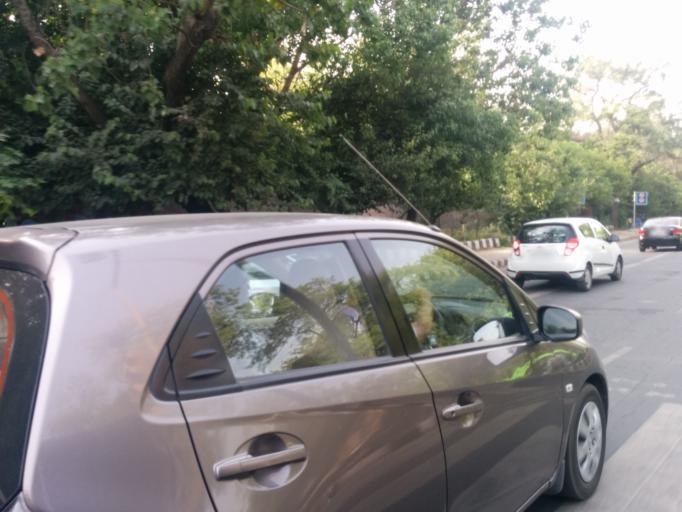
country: IN
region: NCT
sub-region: New Delhi
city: New Delhi
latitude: 28.5395
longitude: 77.1990
